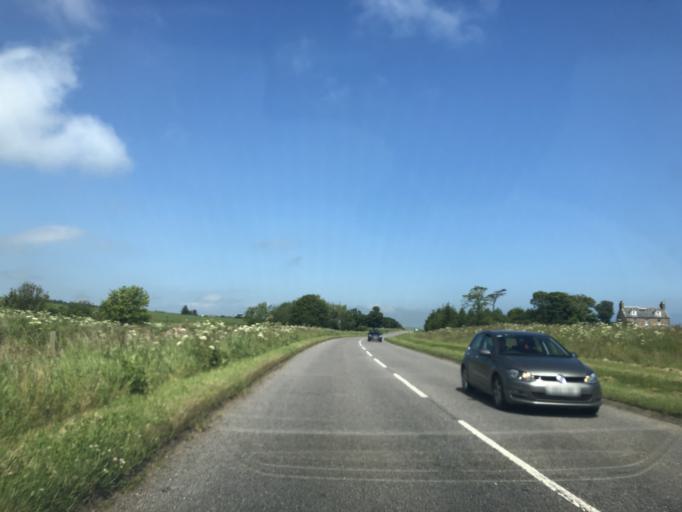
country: GB
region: Scotland
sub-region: Aberdeenshire
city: Stonehaven
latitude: 56.9323
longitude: -2.2080
